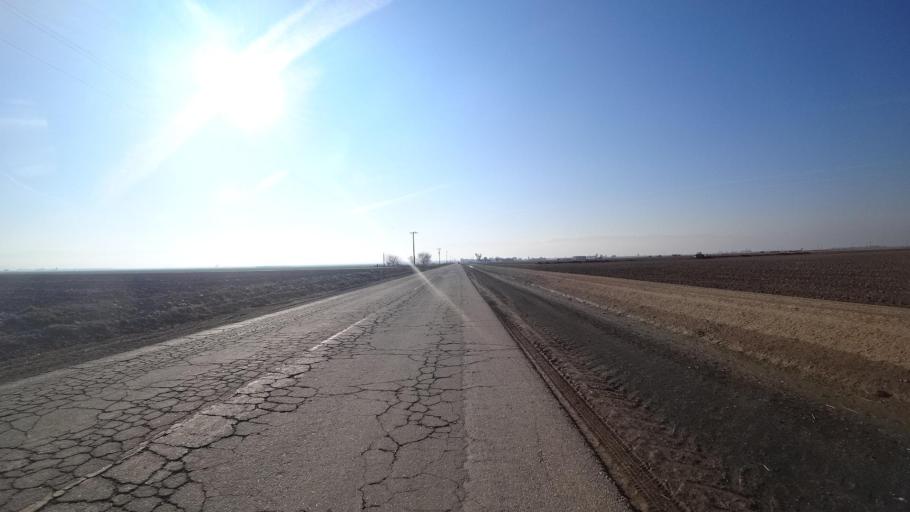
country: US
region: California
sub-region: Kern County
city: Weedpatch
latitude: 35.1741
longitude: -118.9678
